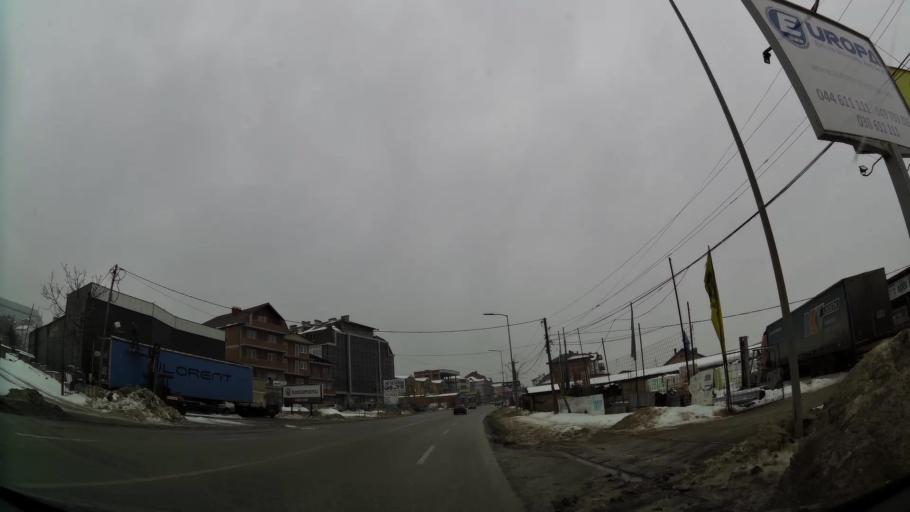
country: XK
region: Pristina
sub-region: Komuna e Prishtines
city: Pristina
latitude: 42.6933
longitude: 21.1605
